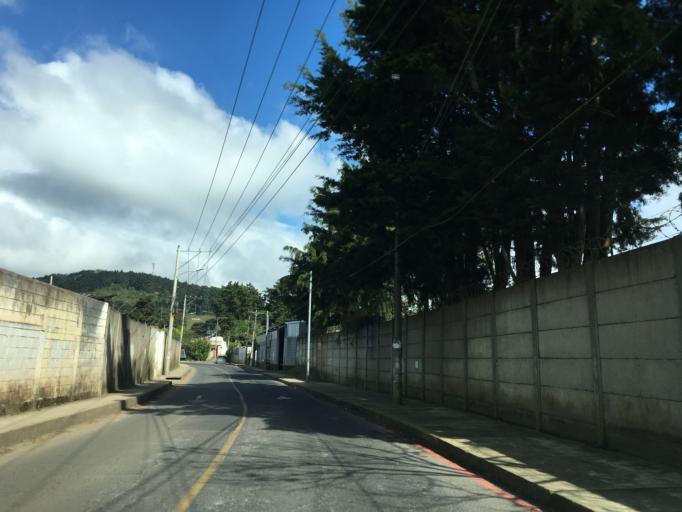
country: GT
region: Guatemala
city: San Jose Pinula
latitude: 14.5461
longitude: -90.4420
